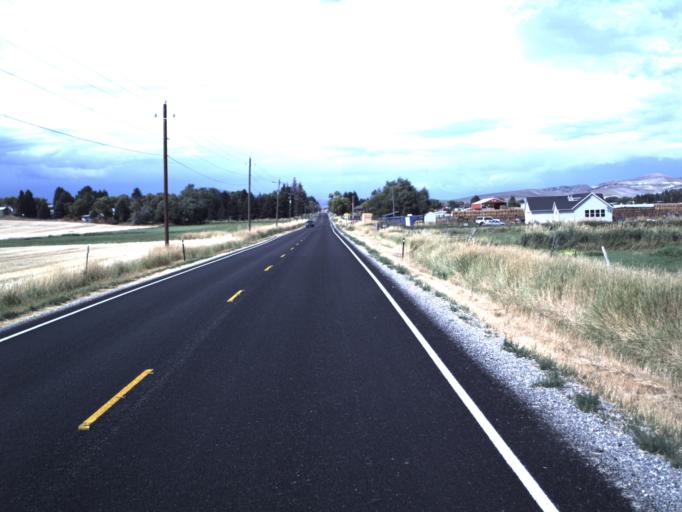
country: US
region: Utah
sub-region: Cache County
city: Benson
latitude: 41.9095
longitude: -112.0454
